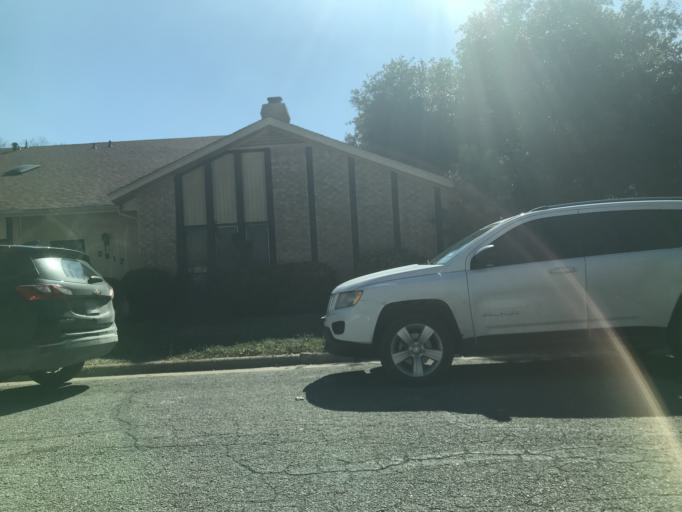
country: US
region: Texas
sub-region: Tom Green County
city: San Angelo
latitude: 31.4297
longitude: -100.4945
